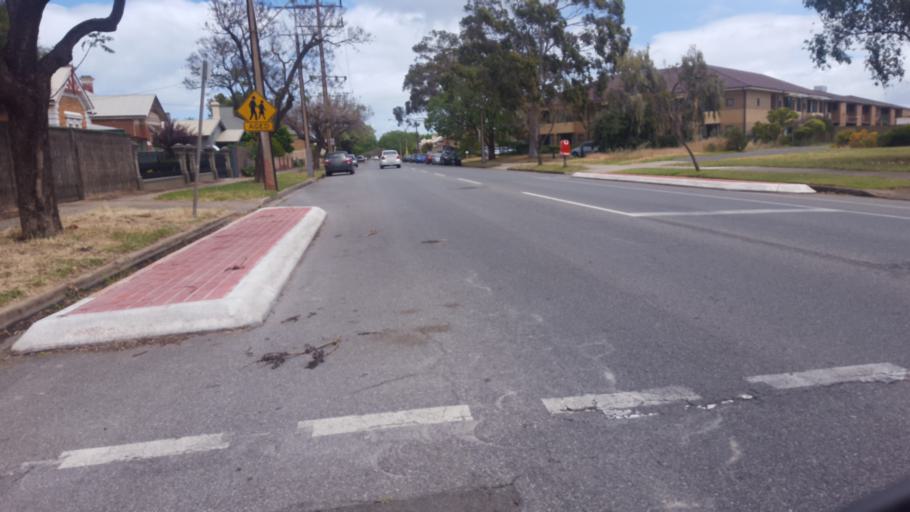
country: AU
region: South Australia
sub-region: Port Adelaide Enfield
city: Alberton
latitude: -34.8606
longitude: 138.5244
